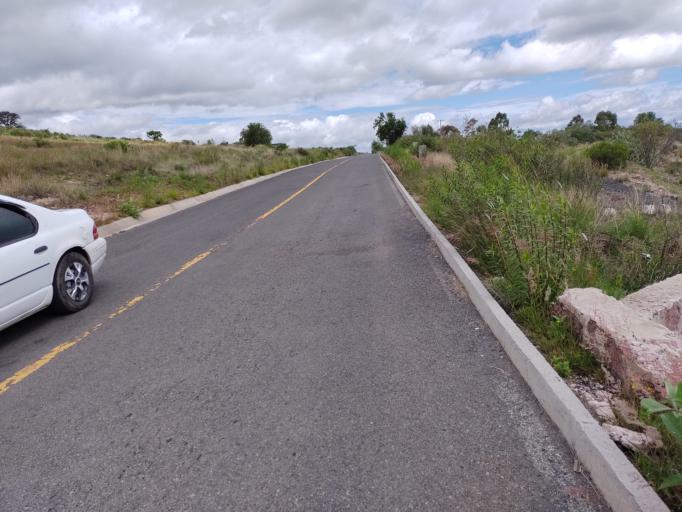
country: MX
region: Mexico
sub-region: Aculco
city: Gunyo Poniente (San Jose Gunyo)
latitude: 20.1124
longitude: -99.8677
